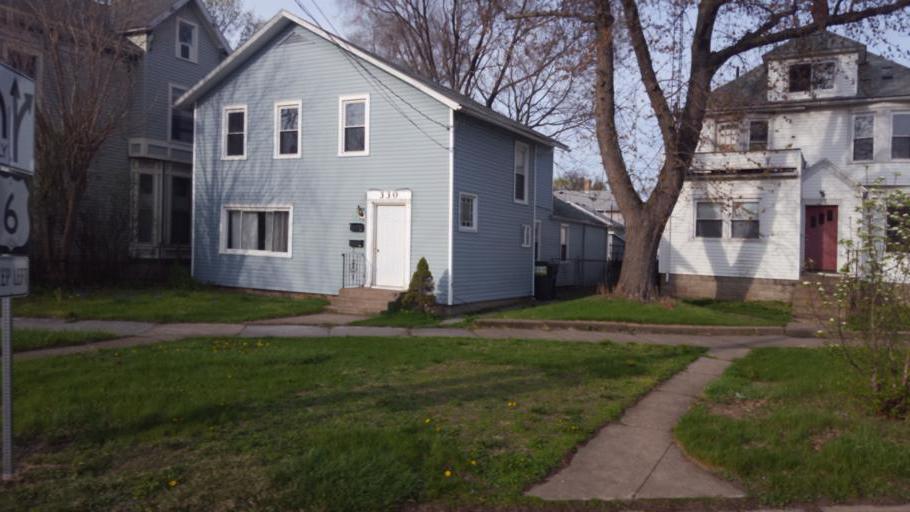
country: US
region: Ohio
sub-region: Erie County
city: Sandusky
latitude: 41.4548
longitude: -82.7083
